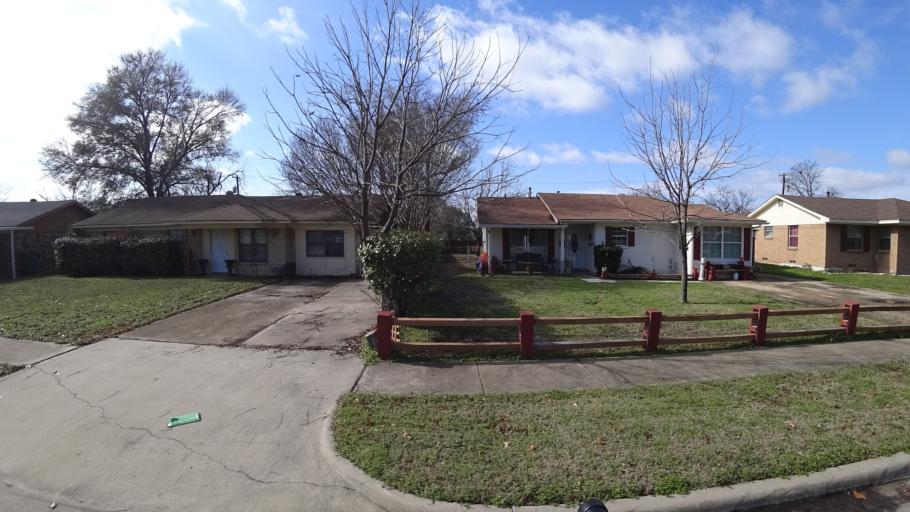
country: US
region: Texas
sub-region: Denton County
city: Lewisville
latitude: 33.0319
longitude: -97.0011
